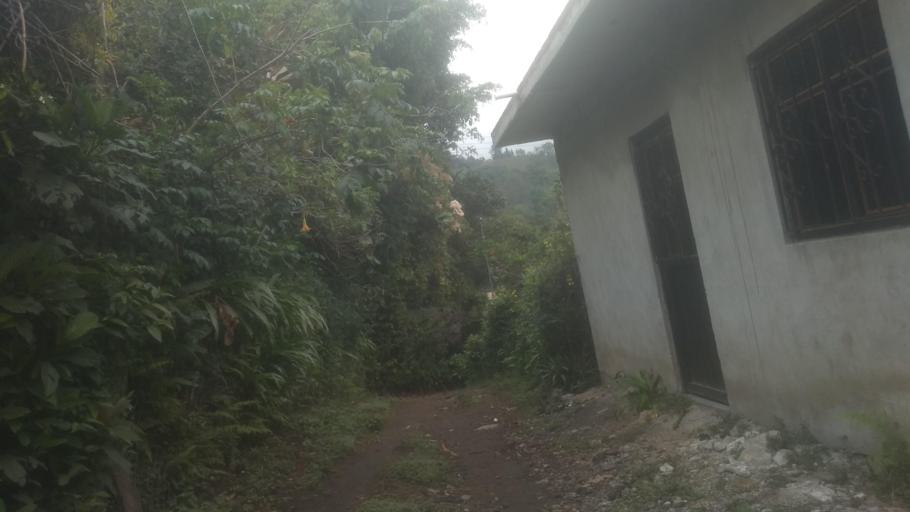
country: MX
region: Veracruz
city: Chocaman
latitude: 18.9860
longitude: -97.0608
